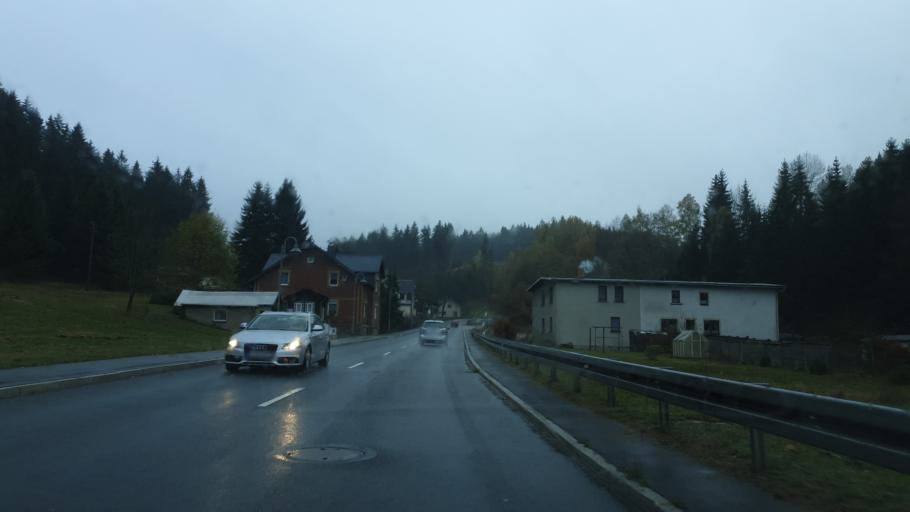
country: DE
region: Saxony
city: Tannenbergsthal
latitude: 50.4306
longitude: 12.4705
